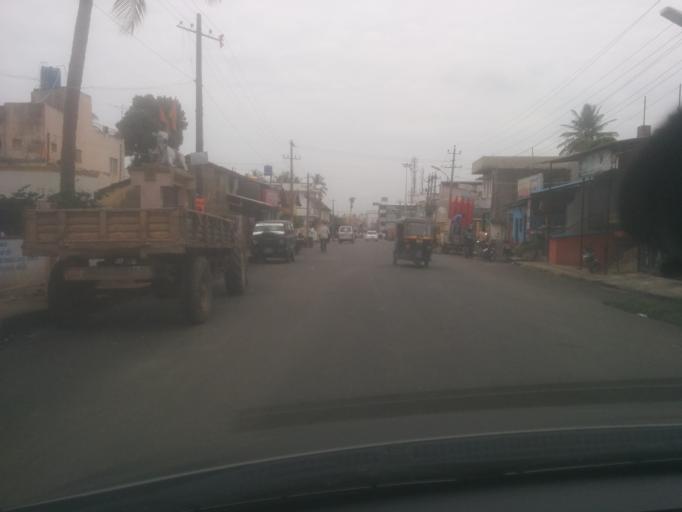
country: IN
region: Karnataka
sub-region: Hassan
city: Belur
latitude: 13.1635
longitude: 75.8628
